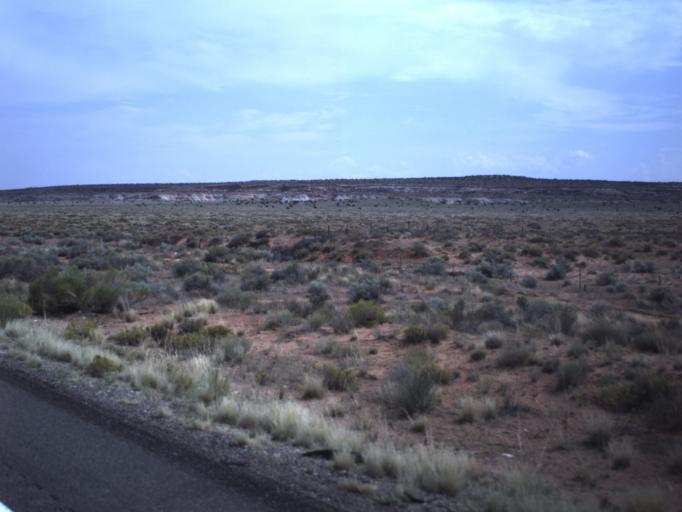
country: US
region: Arizona
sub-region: Coconino County
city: Page
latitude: 37.0953
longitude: -111.7605
